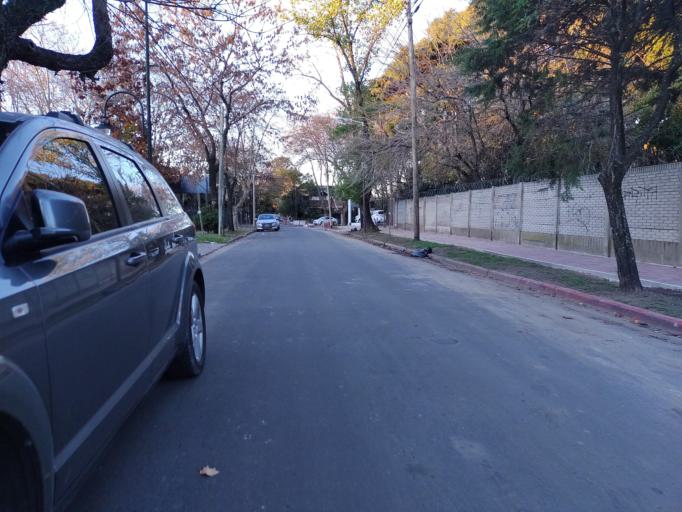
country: AR
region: Buenos Aires
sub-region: Partido de San Isidro
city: San Isidro
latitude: -34.4488
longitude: -58.5380
